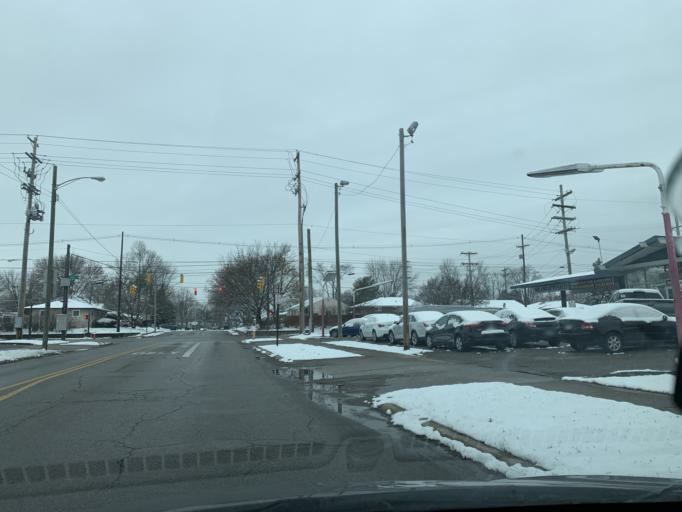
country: US
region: Ohio
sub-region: Franklin County
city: Minerva Park
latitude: 40.0555
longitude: -82.9755
